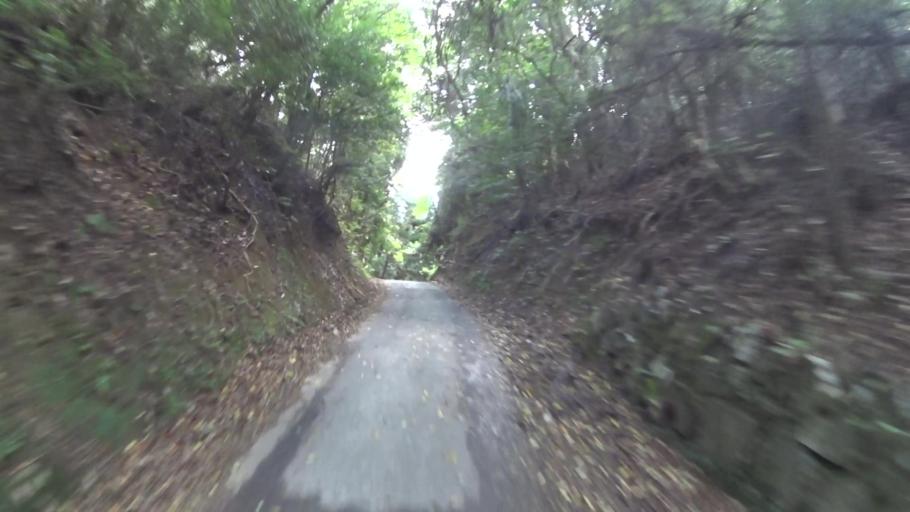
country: JP
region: Shiga Prefecture
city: Otsu-shi
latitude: 34.9451
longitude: 135.8710
